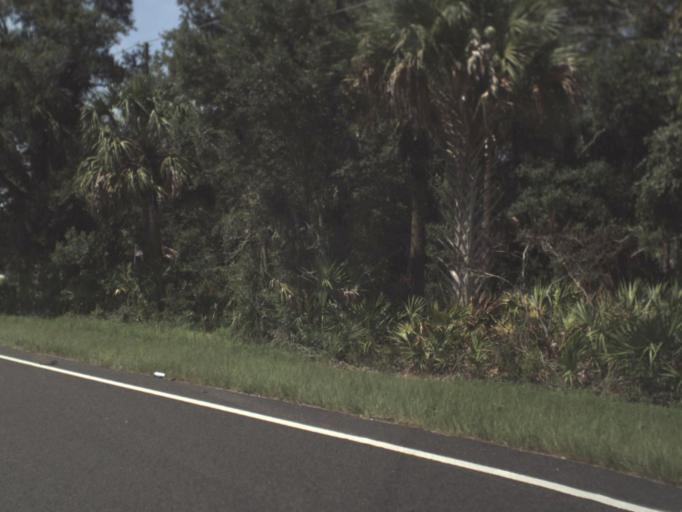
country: US
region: Florida
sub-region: Levy County
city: Inglis
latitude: 28.9734
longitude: -82.6371
